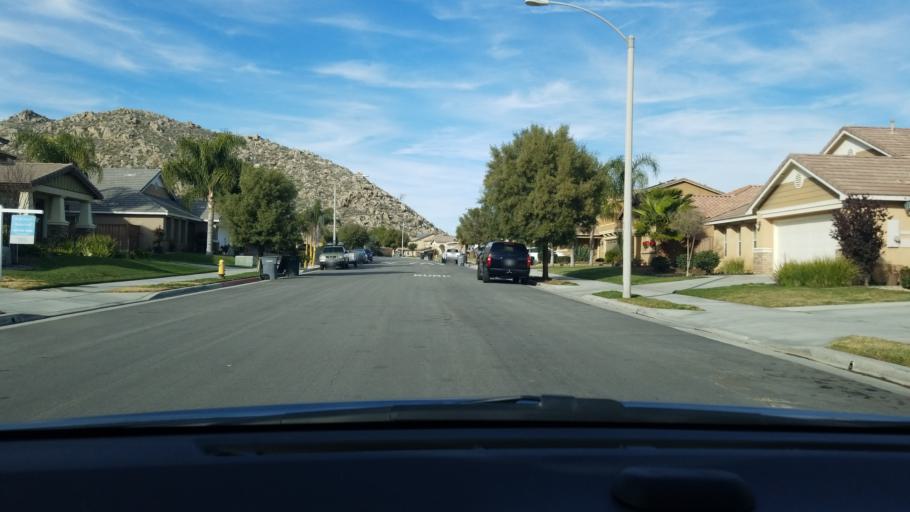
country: US
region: California
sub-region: Riverside County
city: Green Acres
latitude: 33.7944
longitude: -117.0373
